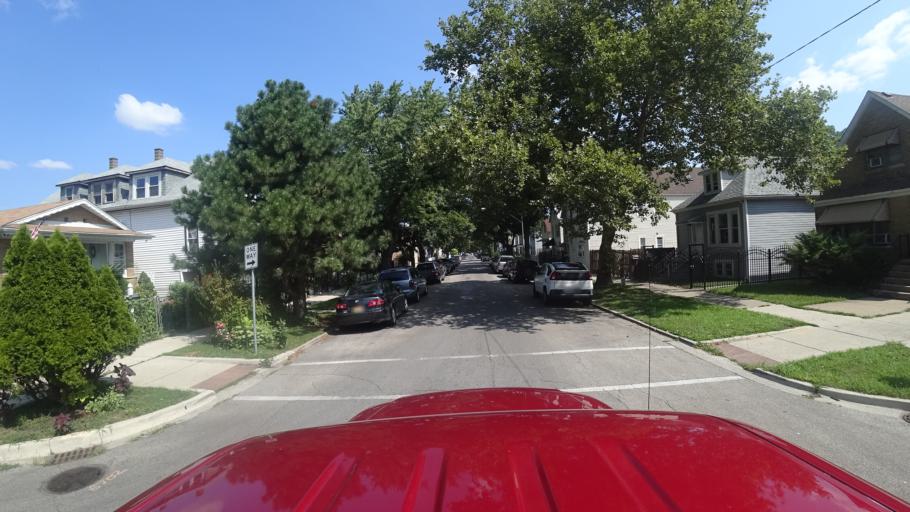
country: US
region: Illinois
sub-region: Cook County
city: Chicago
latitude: 41.7974
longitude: -87.6878
